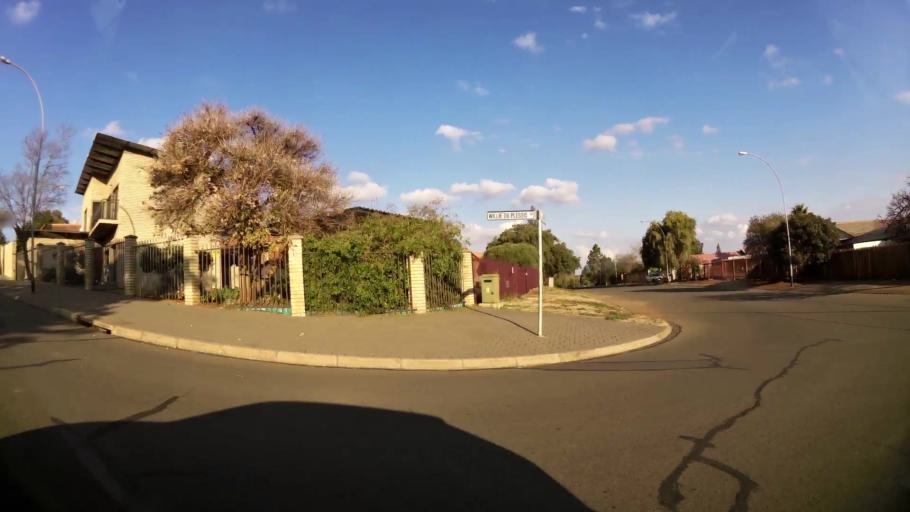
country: ZA
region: Orange Free State
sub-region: Mangaung Metropolitan Municipality
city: Bloemfontein
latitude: -29.1555
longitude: 26.1770
